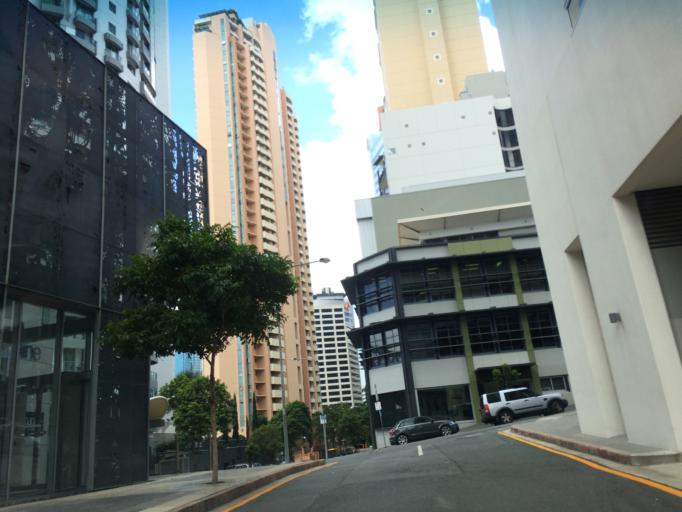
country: AU
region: Queensland
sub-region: Brisbane
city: Fortitude Valley
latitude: -27.4627
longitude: 153.0326
